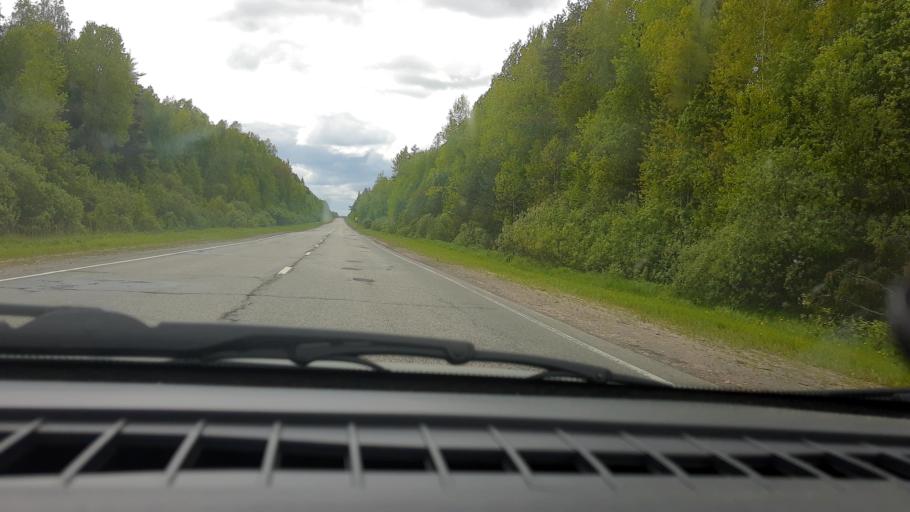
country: RU
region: Nizjnij Novgorod
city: Vladimirskoye
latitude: 56.9385
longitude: 45.0764
